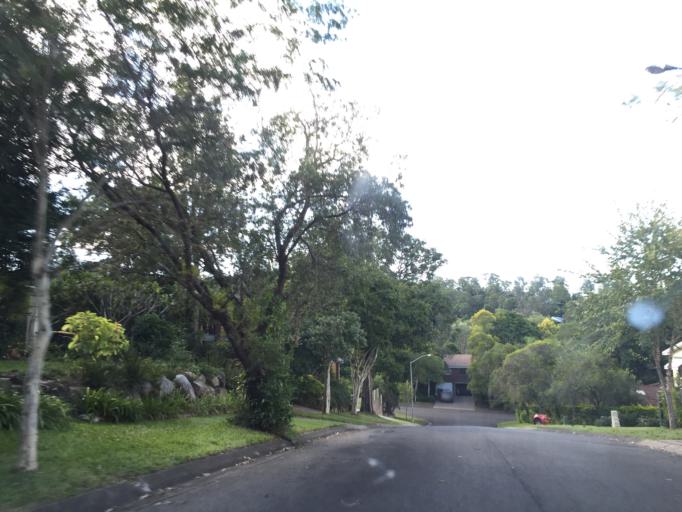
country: AU
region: Queensland
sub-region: Moreton Bay
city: Ferny Hills
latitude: -27.4381
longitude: 152.9305
